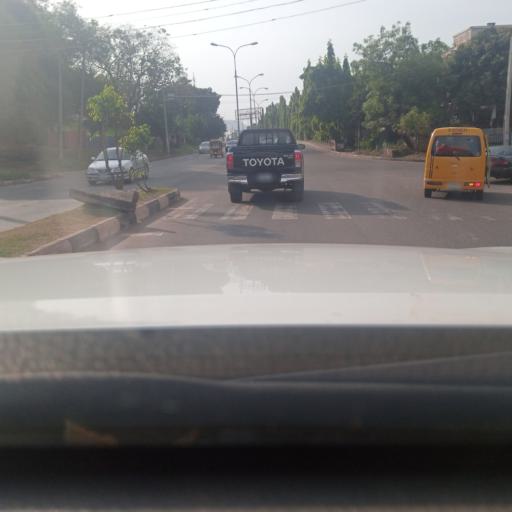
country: NG
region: Enugu
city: Enugu
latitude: 6.4404
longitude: 7.5137
